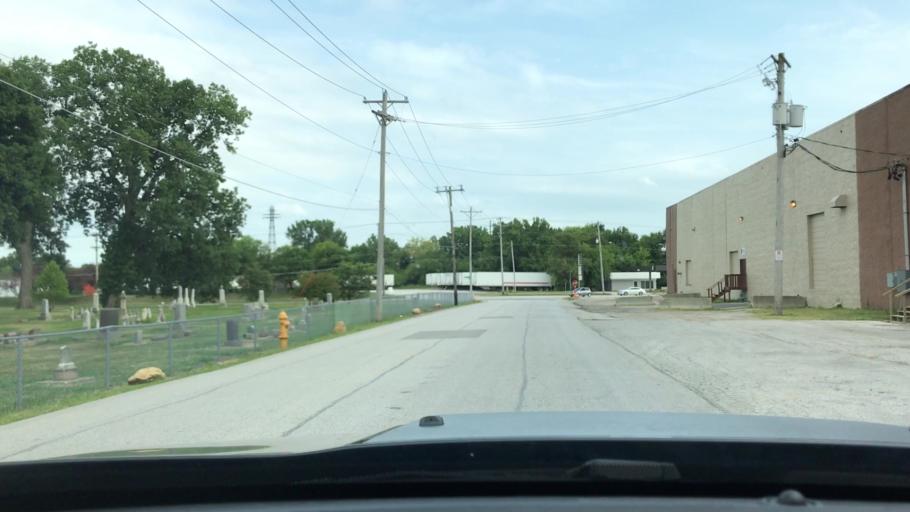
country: US
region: Iowa
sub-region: Scott County
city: Davenport
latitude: 41.5186
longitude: -90.6013
